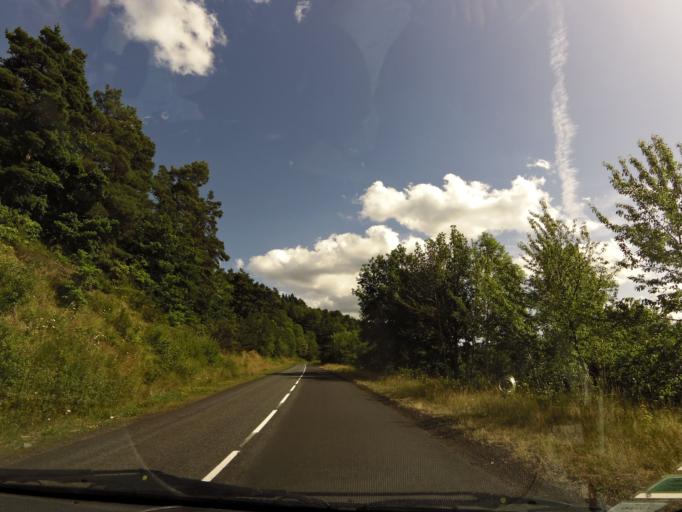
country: FR
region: Auvergne
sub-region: Departement du Puy-de-Dome
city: Aydat
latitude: 45.5647
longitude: 2.9481
